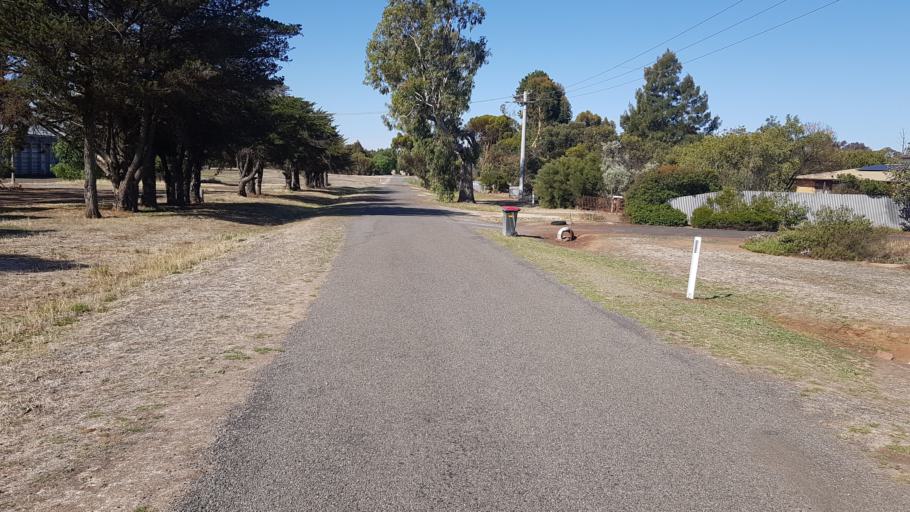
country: AU
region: Victoria
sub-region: Horsham
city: Horsham
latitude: -36.7457
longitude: 141.9393
